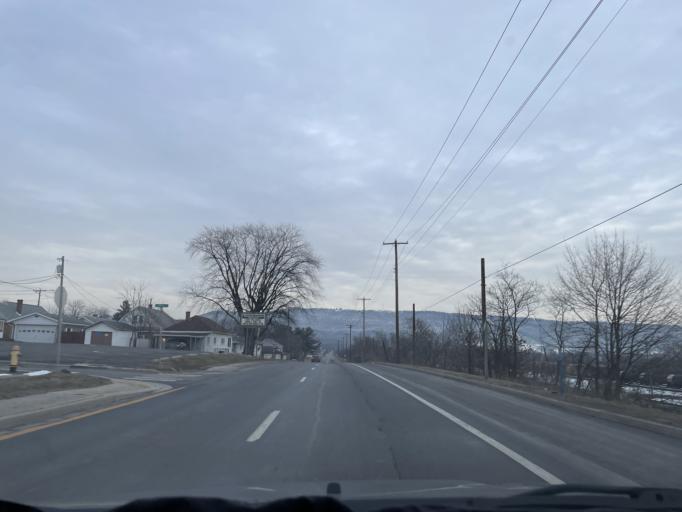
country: US
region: Maryland
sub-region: Allegany County
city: Cumberland
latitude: 39.6315
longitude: -78.7611
